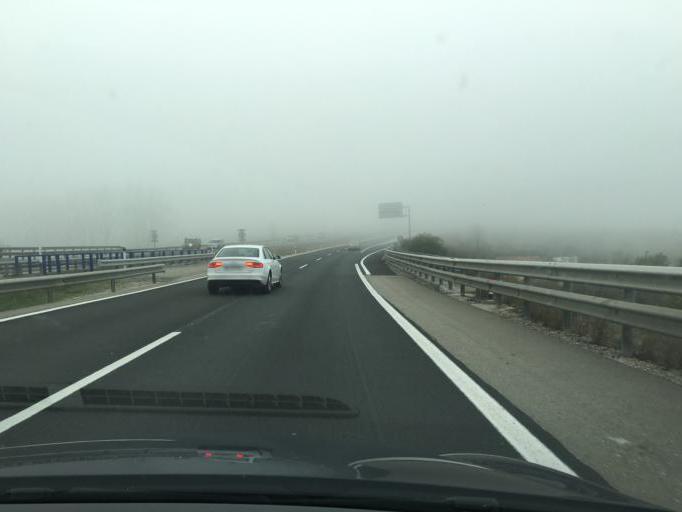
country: ES
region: Castille and Leon
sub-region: Provincia de Burgos
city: Pancorbo
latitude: 42.6270
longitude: -3.1099
